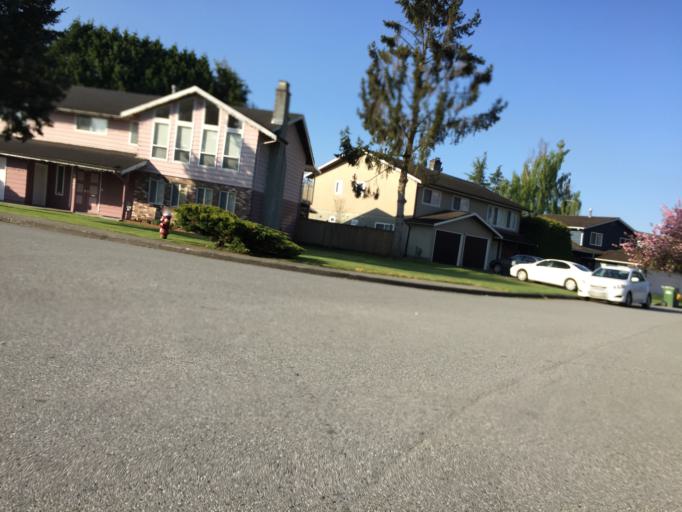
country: CA
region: British Columbia
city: Richmond
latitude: 49.1455
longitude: -123.1282
